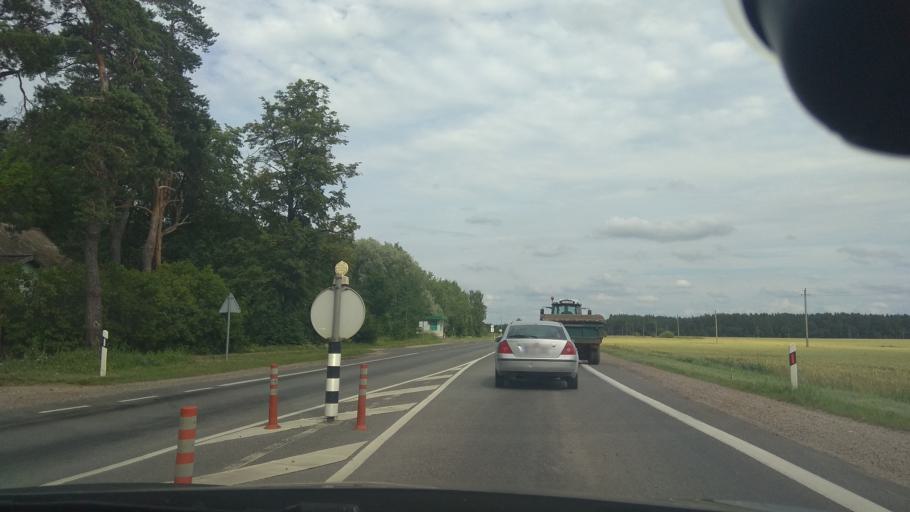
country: LT
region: Panevezys
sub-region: Panevezys City
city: Panevezys
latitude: 55.7343
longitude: 24.2432
